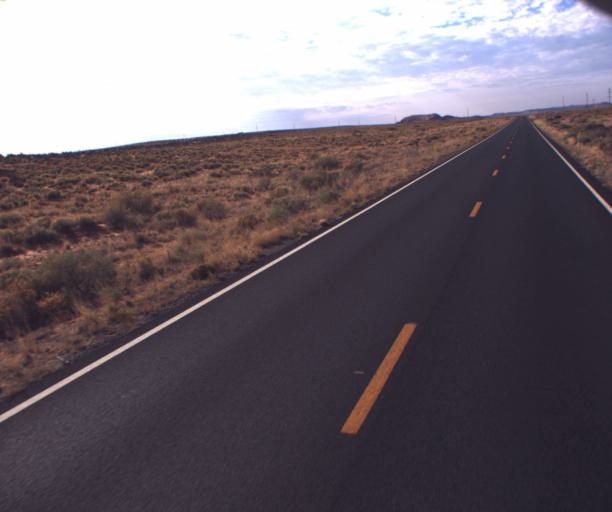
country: US
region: Arizona
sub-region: Apache County
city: Many Farms
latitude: 36.8008
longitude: -109.6488
